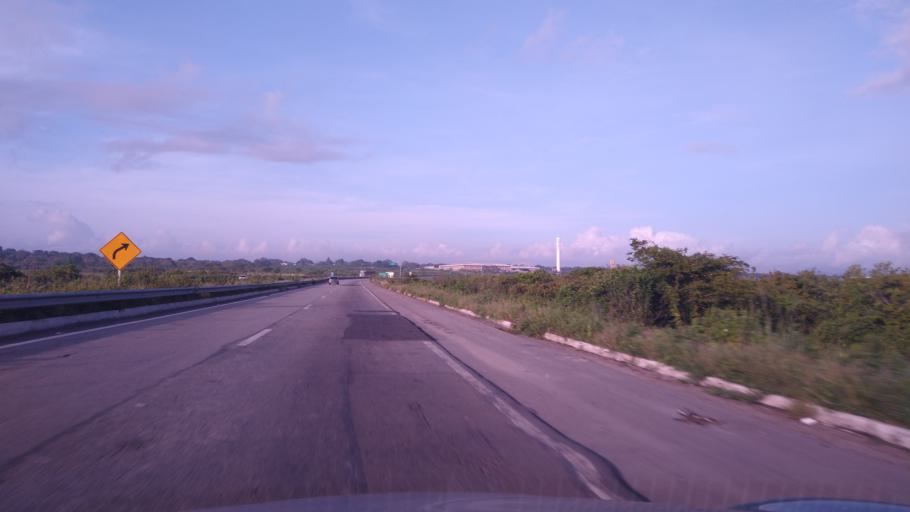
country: BR
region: Ceara
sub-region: Pacajus
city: Pacajus
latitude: -4.1585
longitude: -38.4830
